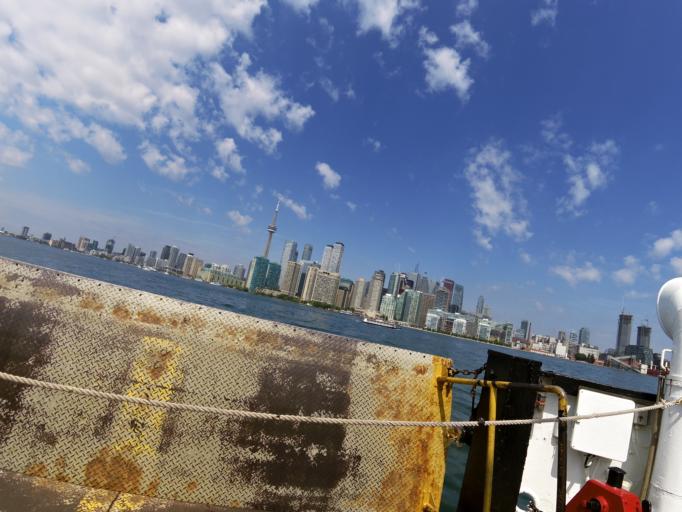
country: CA
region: Ontario
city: Toronto
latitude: 43.6341
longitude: -79.3663
